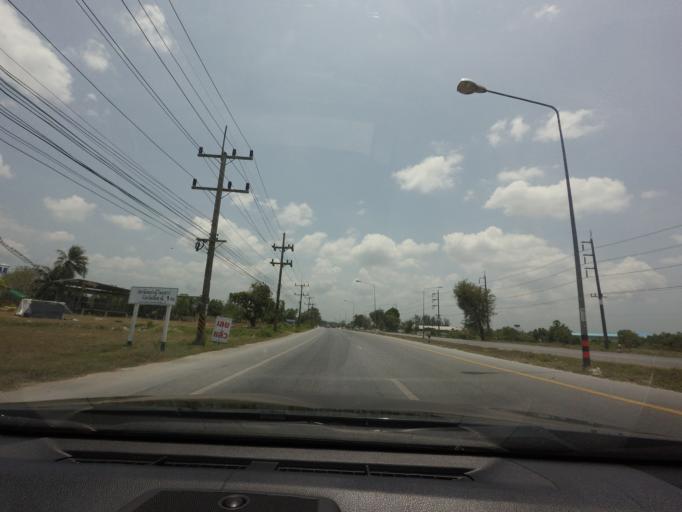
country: TH
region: Pattani
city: Pattani
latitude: 6.8644
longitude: 101.2718
